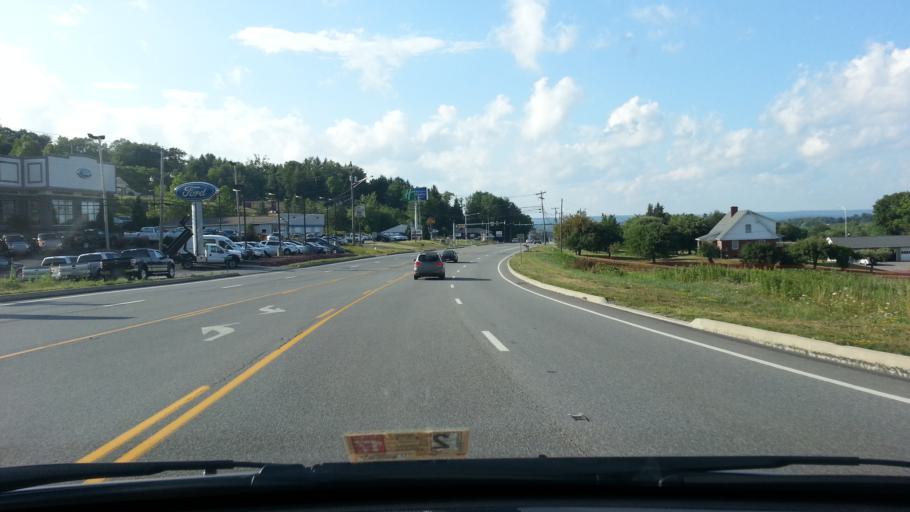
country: US
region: Pennsylvania
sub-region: Elk County
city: Saint Marys
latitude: 41.4011
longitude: -78.5602
